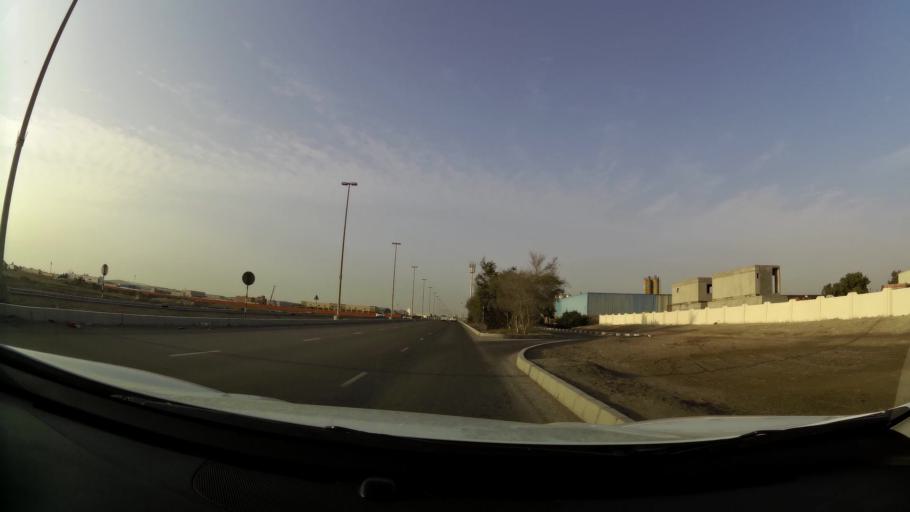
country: AE
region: Abu Dhabi
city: Abu Dhabi
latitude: 24.3376
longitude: 54.5029
